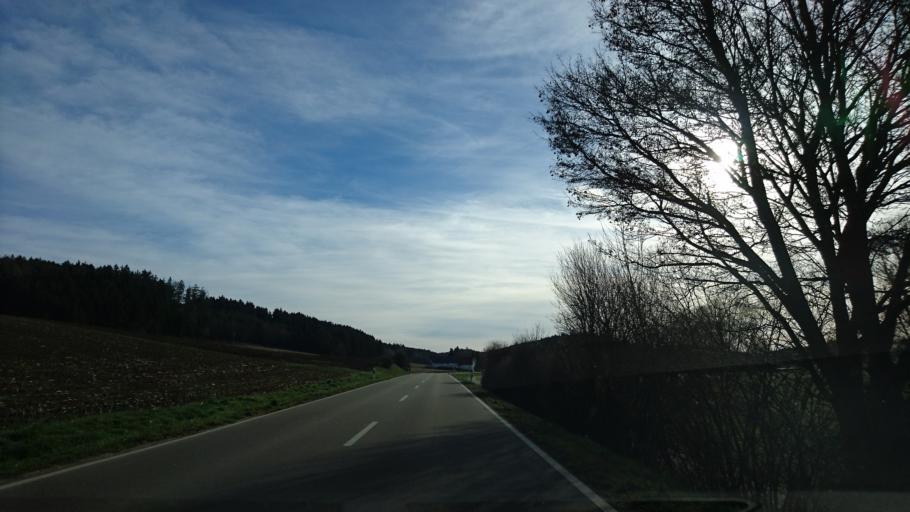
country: DE
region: Bavaria
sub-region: Swabia
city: Laugna
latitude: 48.5249
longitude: 10.7207
